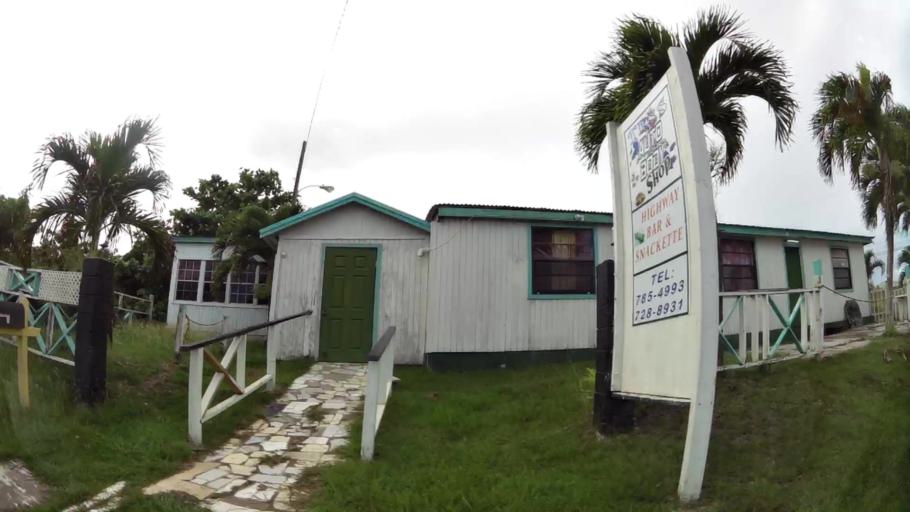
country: AG
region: Saint John
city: Potters Village
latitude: 17.0956
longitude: -61.8131
